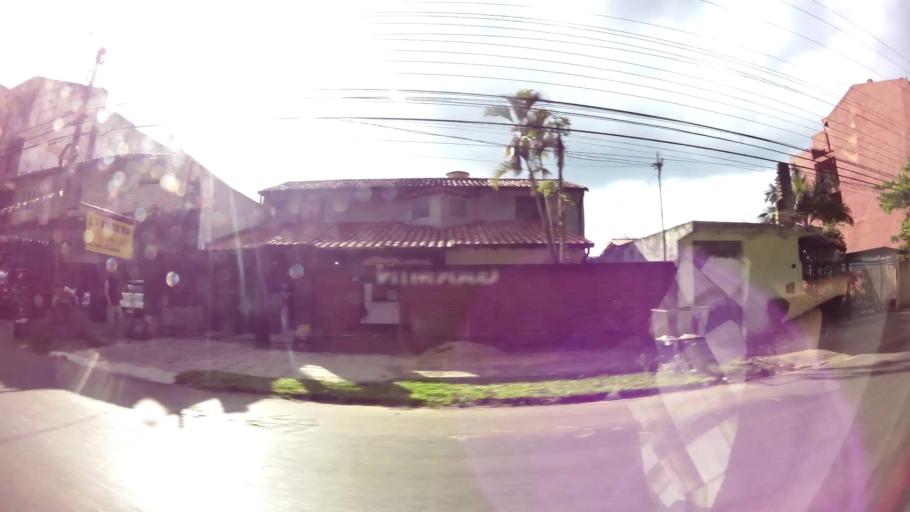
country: PY
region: Central
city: Villa Elisa
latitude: -25.3396
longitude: -57.5642
